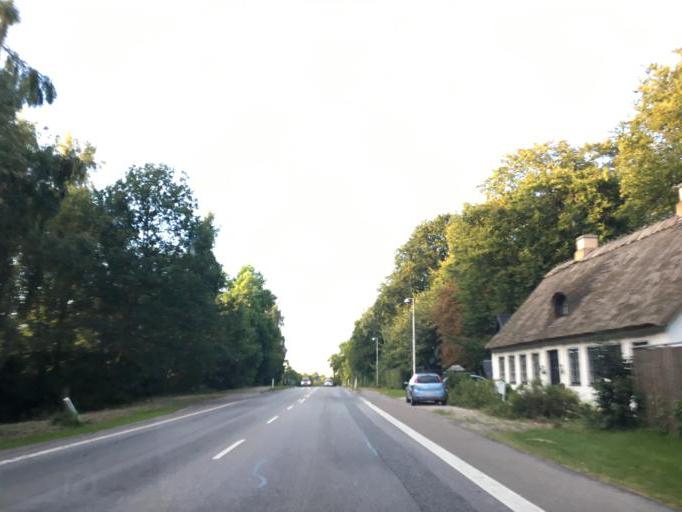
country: DK
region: Capital Region
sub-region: Horsholm Kommune
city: Horsholm
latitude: 55.8711
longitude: 12.4980
